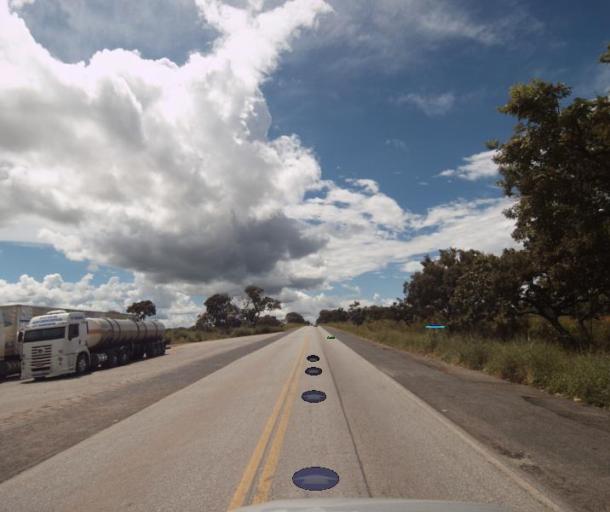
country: BR
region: Goias
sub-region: Uruacu
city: Uruacu
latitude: -14.0239
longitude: -49.0875
